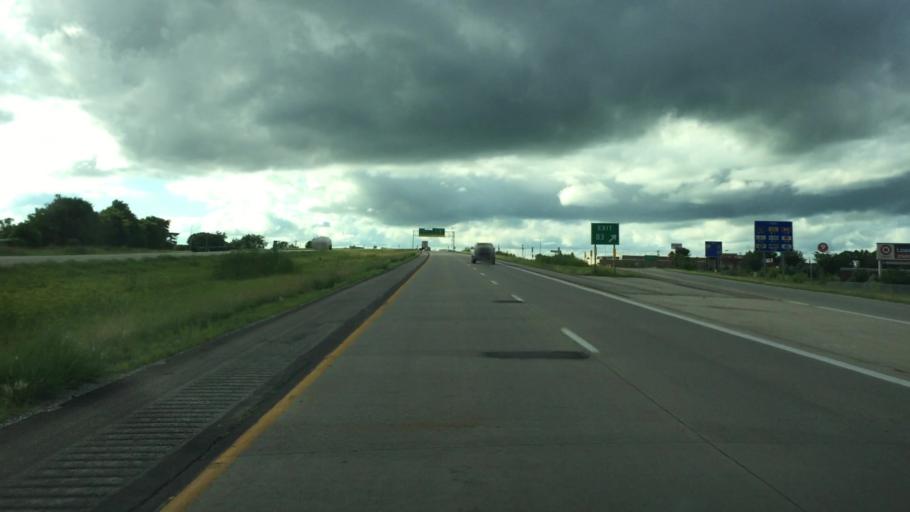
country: US
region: Iowa
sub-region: Polk County
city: Altoona
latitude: 41.6407
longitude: -93.5079
